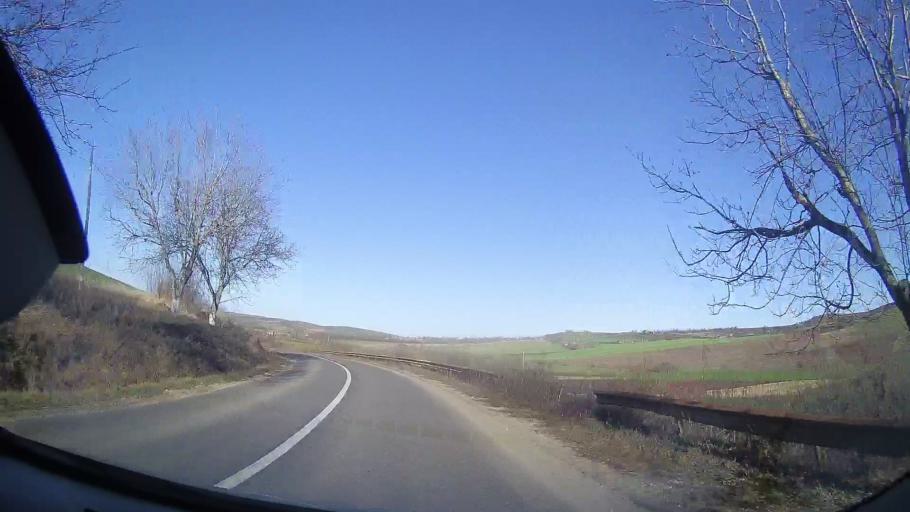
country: RO
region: Mures
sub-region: Comuna Sarmasu
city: Balda
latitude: 46.7361
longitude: 24.1494
